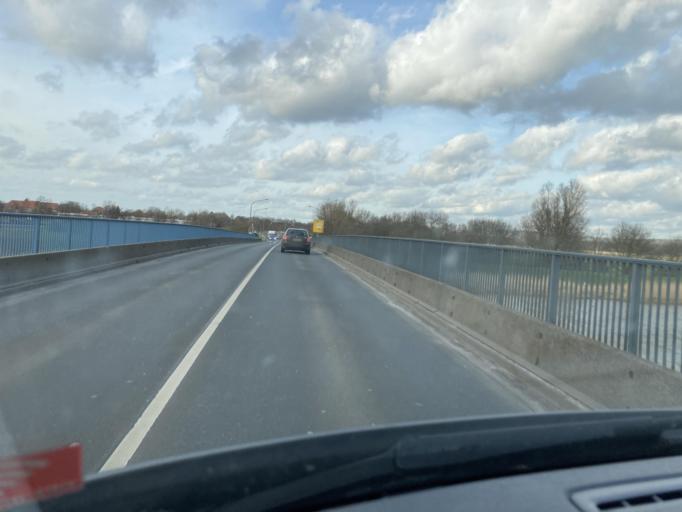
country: DE
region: Lower Saxony
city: Leer
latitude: 53.2203
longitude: 7.4835
